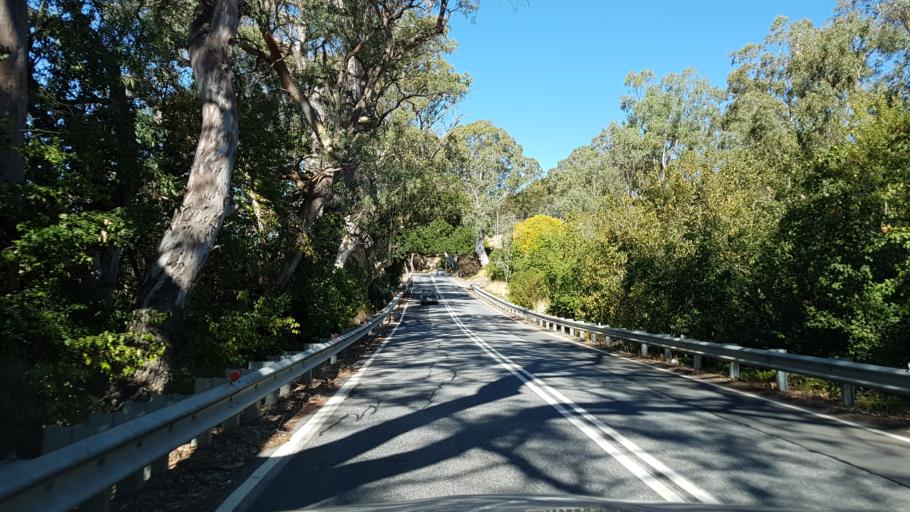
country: AU
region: South Australia
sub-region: Adelaide Hills
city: Gumeracha
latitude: -34.8201
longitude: 138.9054
